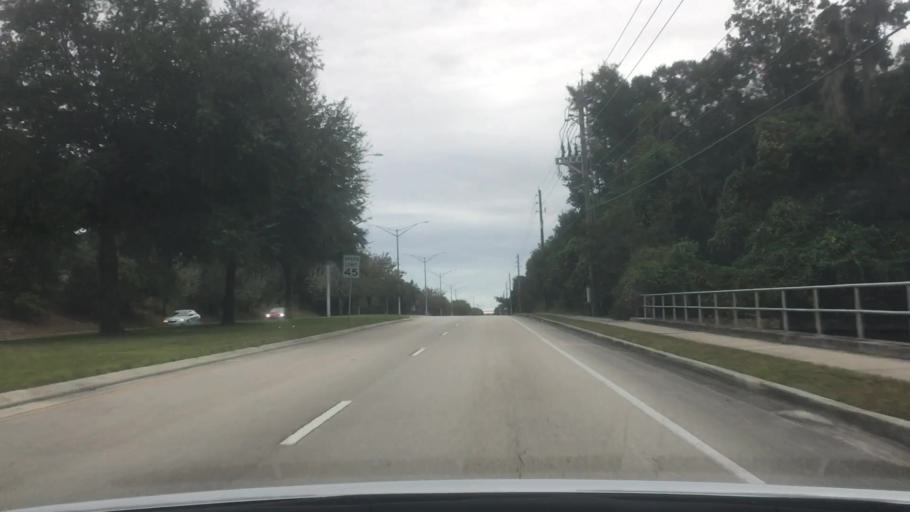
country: US
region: Florida
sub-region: Duval County
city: Jacksonville
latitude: 30.3456
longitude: -81.5293
